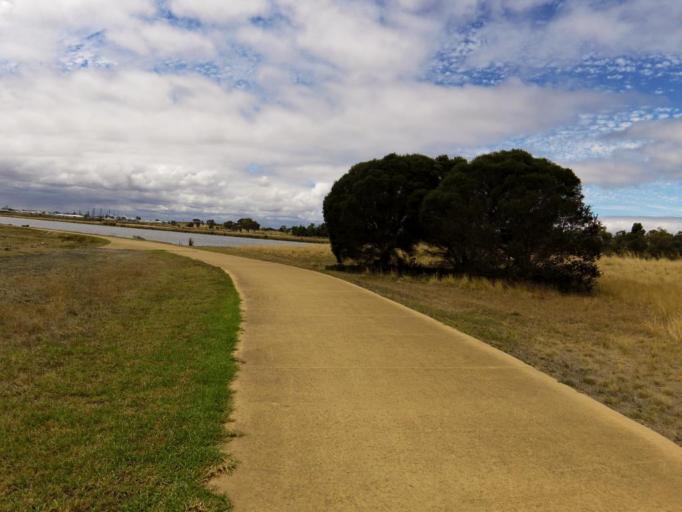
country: AU
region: Victoria
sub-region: Hobsons Bay
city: Altona Meadows
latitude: -37.8756
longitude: 144.7977
